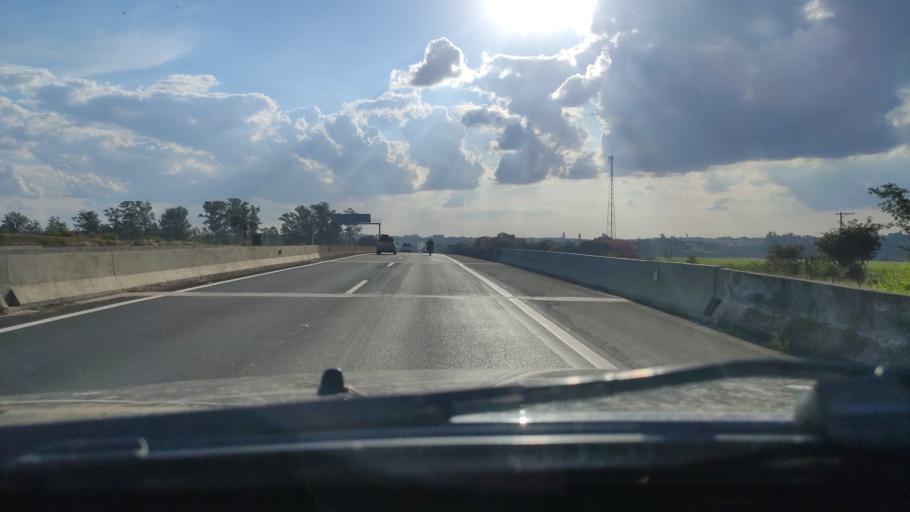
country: BR
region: Sao Paulo
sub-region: Mogi-Mirim
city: Mogi Mirim
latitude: -22.4557
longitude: -46.9160
